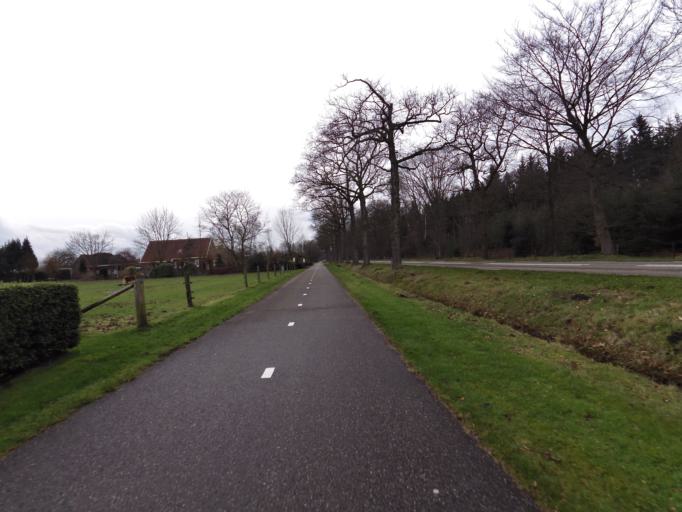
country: NL
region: Gelderland
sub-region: Oude IJsselstreek
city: Wisch
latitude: 51.9534
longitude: 6.3843
